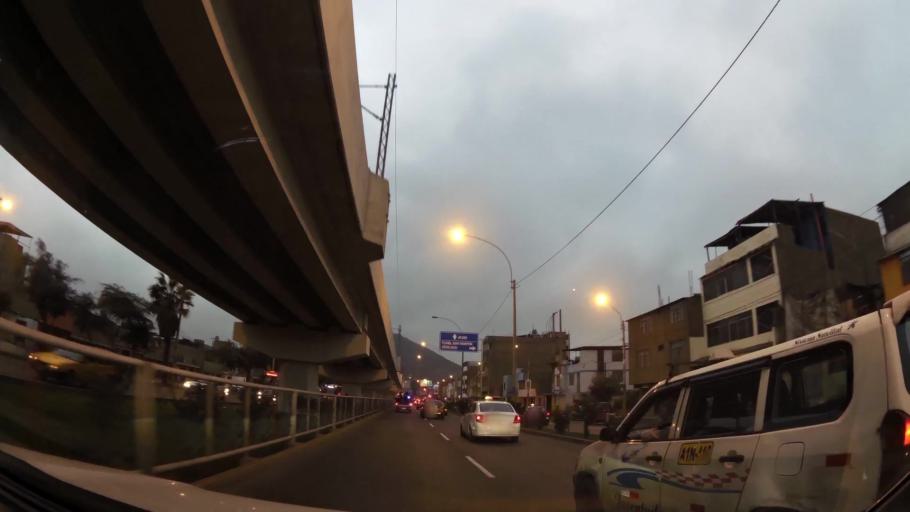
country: PE
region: Lima
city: Lima
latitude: -12.0240
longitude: -77.0087
